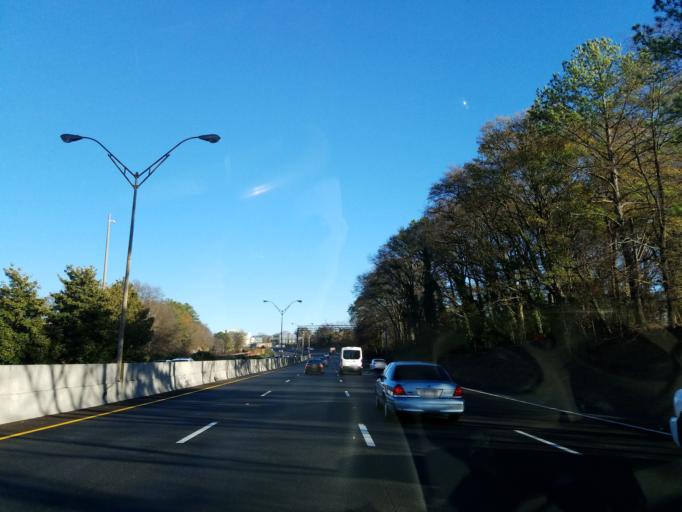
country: US
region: Georgia
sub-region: Fulton County
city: Atlanta
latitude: 33.7517
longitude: -84.4585
